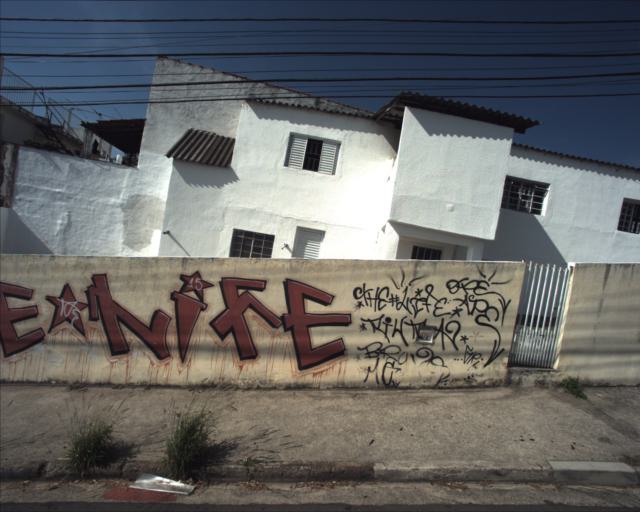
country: BR
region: Sao Paulo
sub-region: Sorocaba
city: Sorocaba
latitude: -23.4858
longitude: -47.4607
